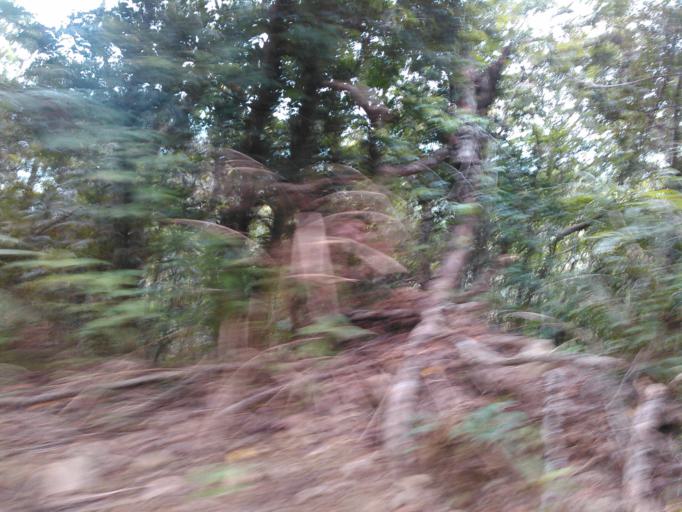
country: TW
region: Taiwan
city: Hengchun
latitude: 22.2666
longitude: 120.8207
